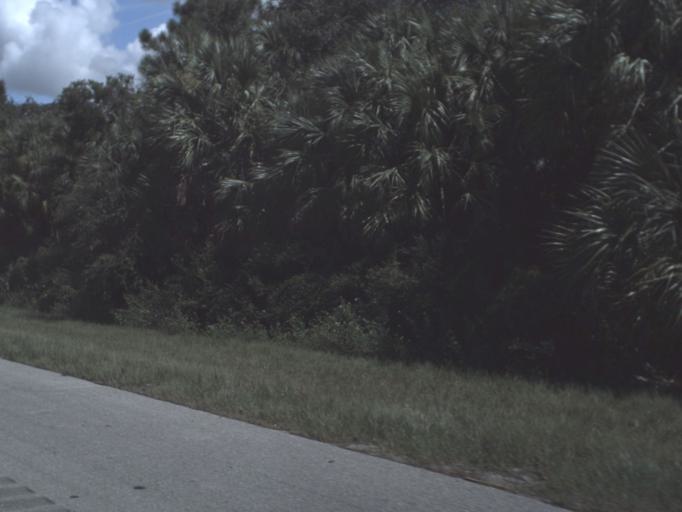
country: US
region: Florida
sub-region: Sarasota County
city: Osprey
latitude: 27.2188
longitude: -82.4473
